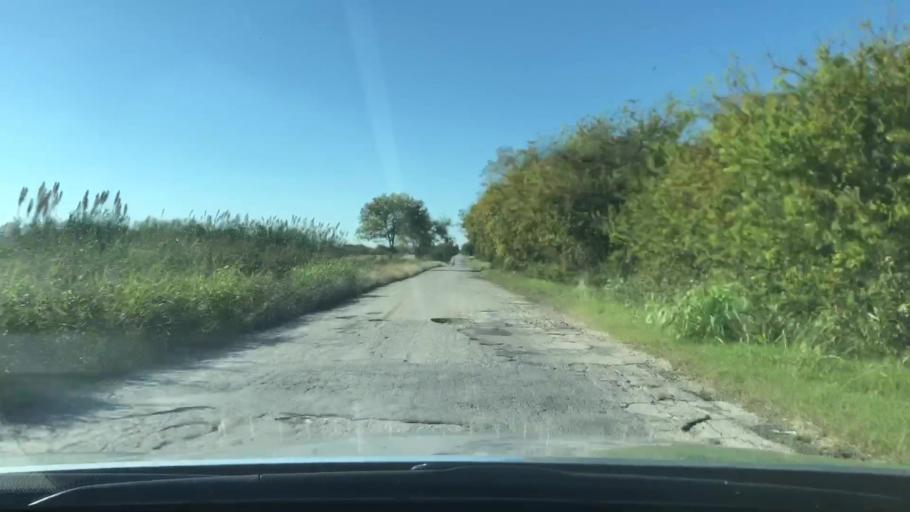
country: US
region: Texas
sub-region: Bexar County
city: Converse
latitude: 29.4660
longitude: -98.2946
